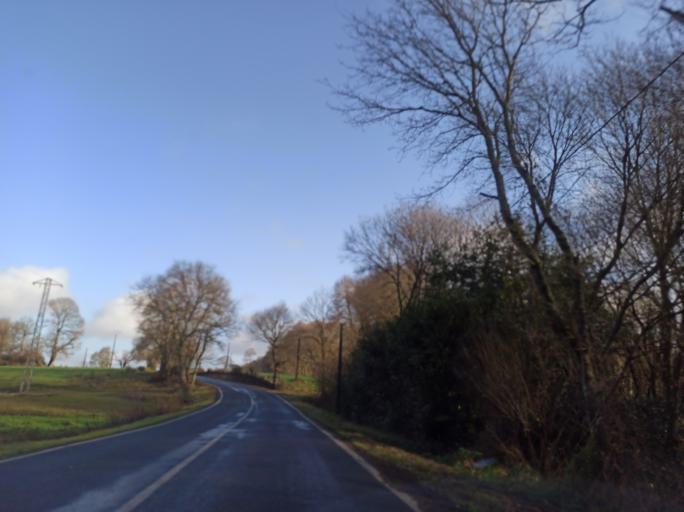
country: ES
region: Galicia
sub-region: Provincia da Coruna
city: Curtis
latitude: 43.0932
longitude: -7.9929
